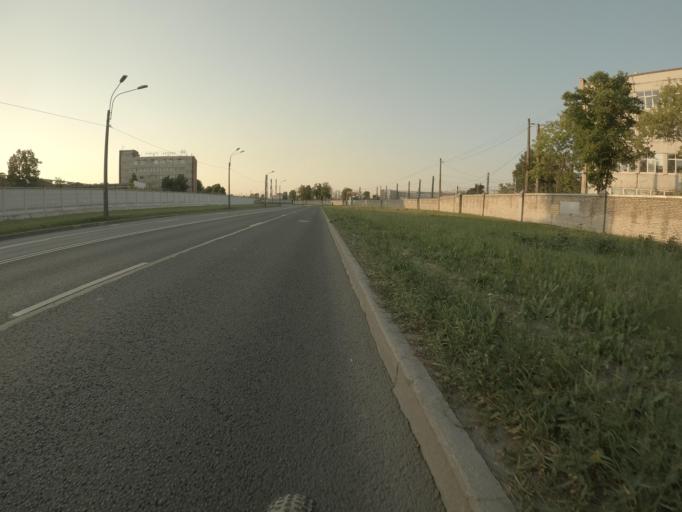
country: RU
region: St.-Petersburg
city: Avtovo
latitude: 59.8566
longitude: 30.2827
